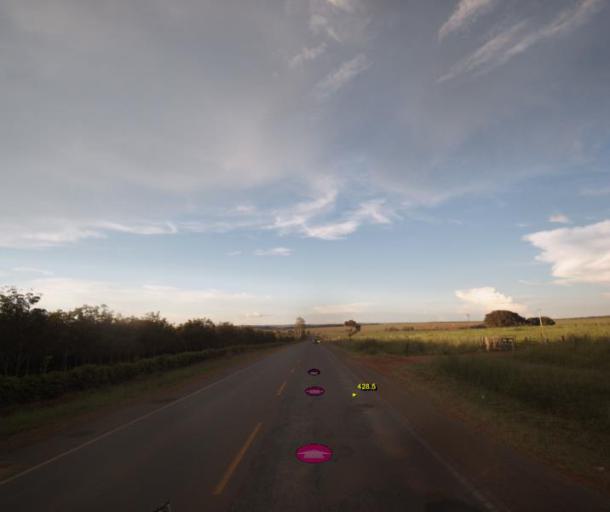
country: BR
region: Goias
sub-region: Anapolis
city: Anapolis
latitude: -16.1945
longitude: -48.9074
